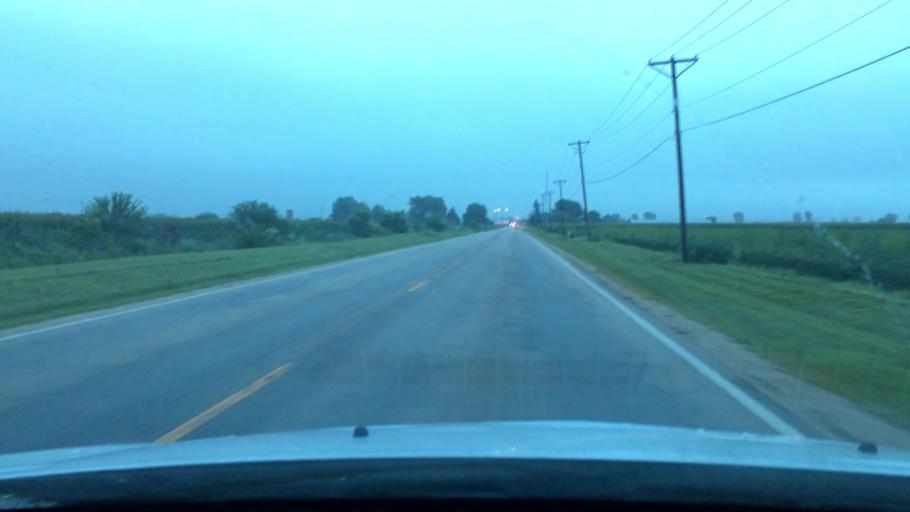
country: US
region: Illinois
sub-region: Ogle County
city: Rochelle
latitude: 41.9219
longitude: -89.0422
